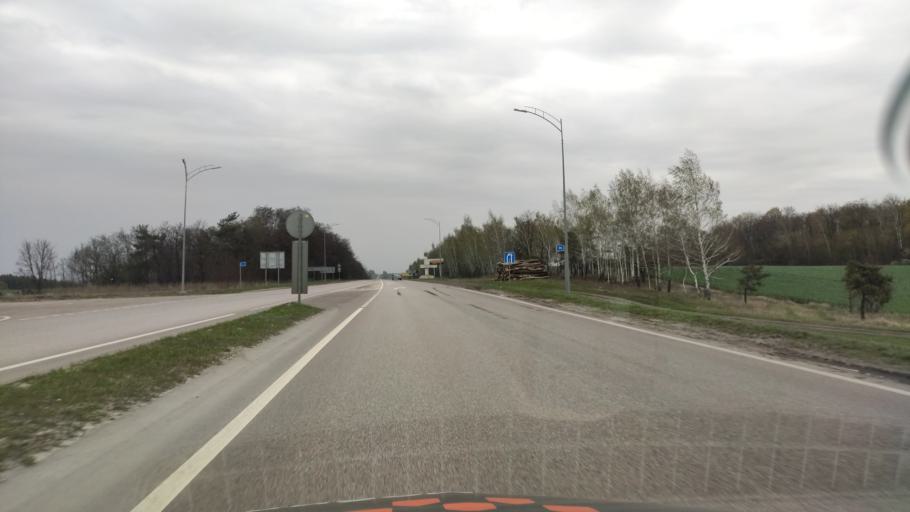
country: RU
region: Belgorod
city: Staryy Oskol
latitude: 51.4272
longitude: 37.8967
